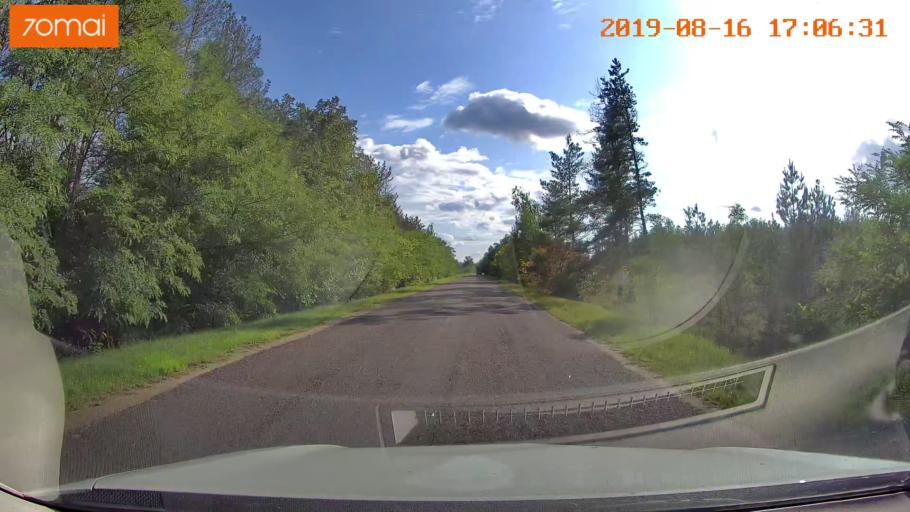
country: BY
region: Mogilev
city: Hlusha
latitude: 53.2263
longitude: 28.9323
